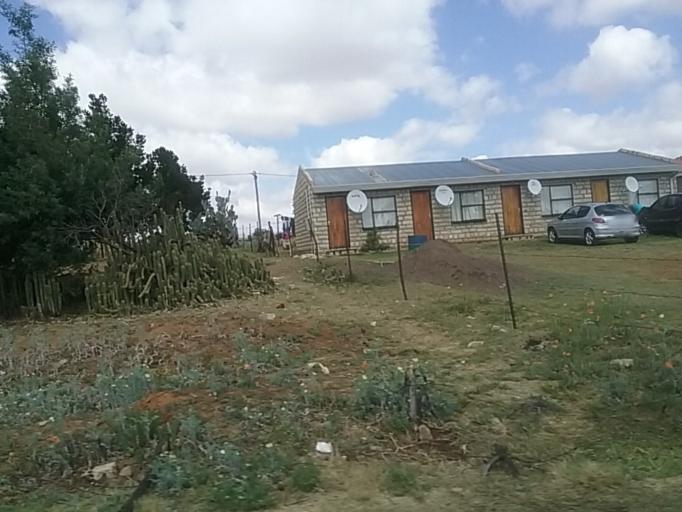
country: LS
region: Berea
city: Teyateyaneng
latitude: -29.1375
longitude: 27.7347
